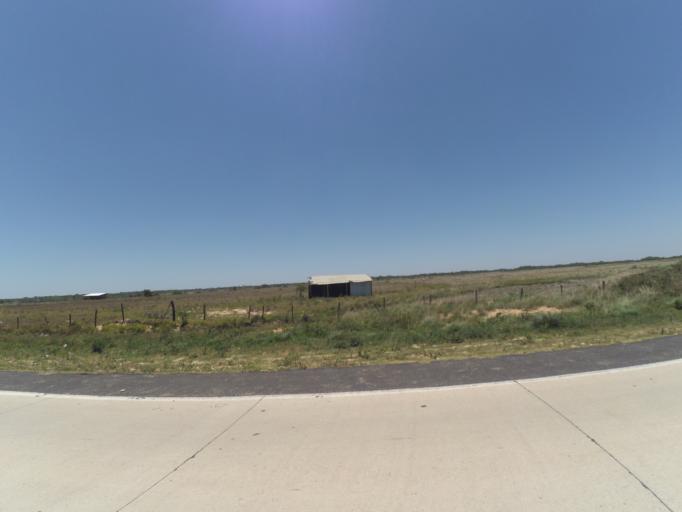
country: BO
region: Santa Cruz
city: Santa Cruz de la Sierra
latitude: -17.7992
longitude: -63.2756
